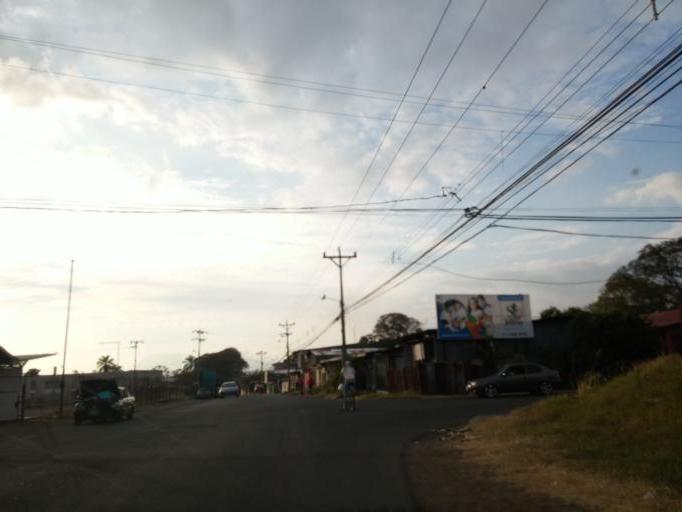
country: CR
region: Alajuela
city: Alajuela
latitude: 10.0054
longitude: -84.2297
